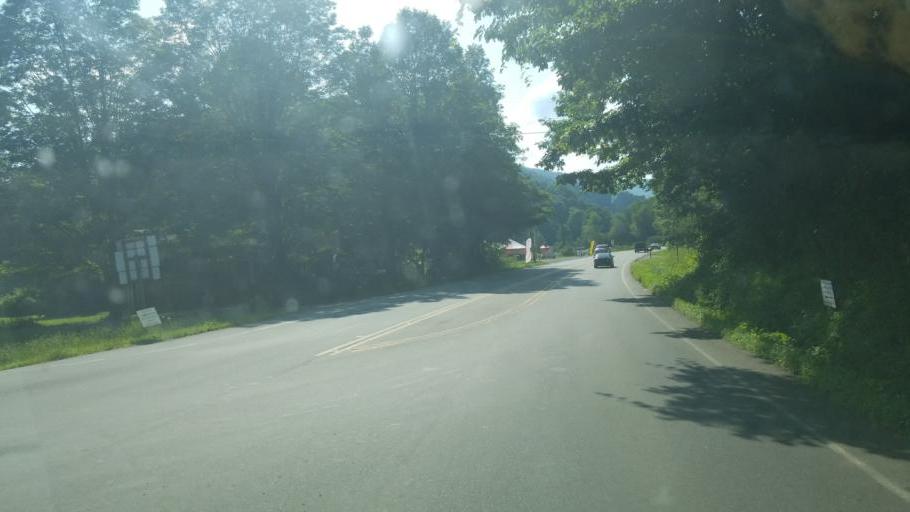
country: US
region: North Carolina
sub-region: Avery County
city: Newland
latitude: 36.1556
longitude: -81.9687
